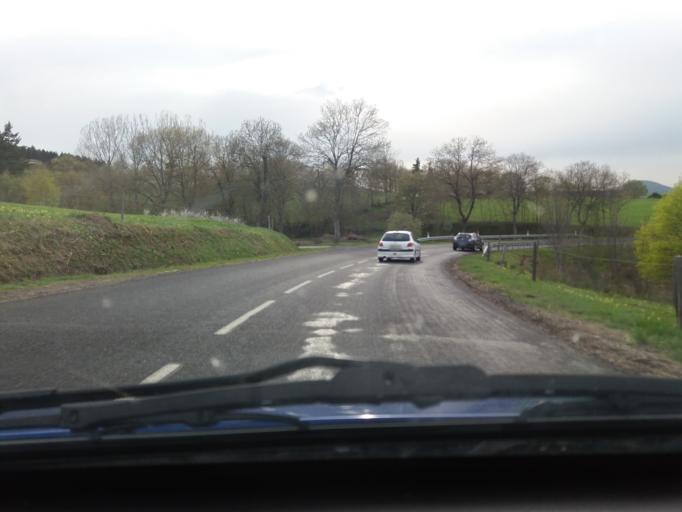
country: FR
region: Auvergne
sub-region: Departement de la Haute-Loire
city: Yssingeaux
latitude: 45.1249
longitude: 4.1531
